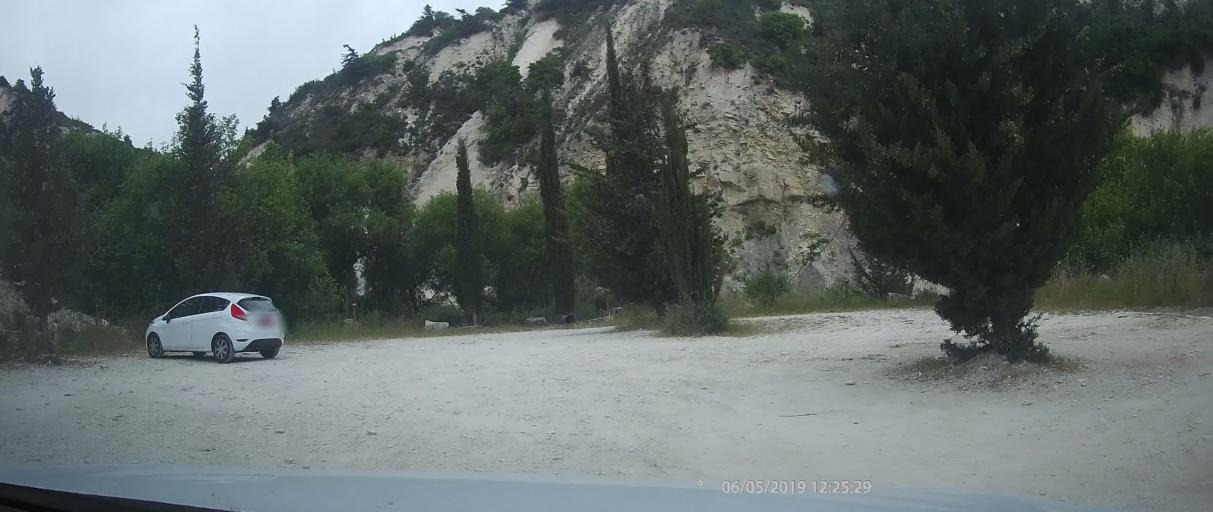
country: CY
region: Pafos
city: Tala
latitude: 34.8705
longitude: 32.4347
